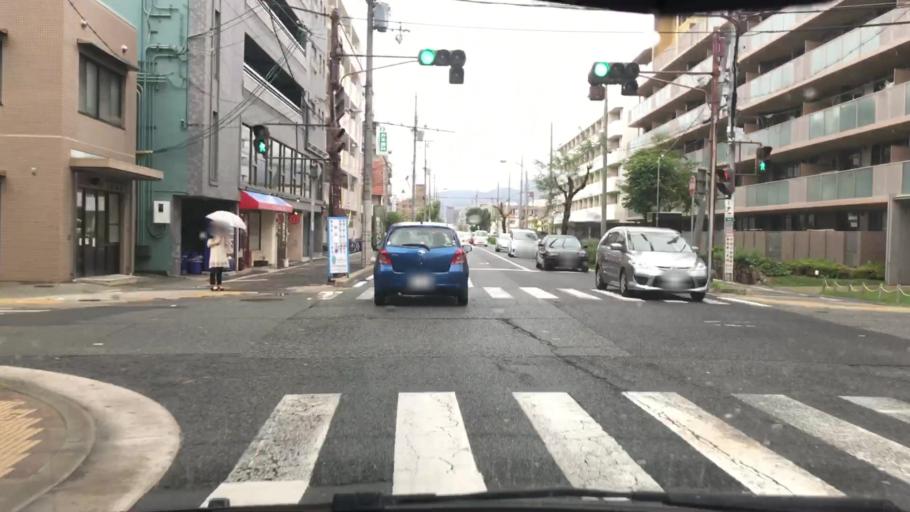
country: JP
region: Hyogo
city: Nishinomiya-hama
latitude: 34.7424
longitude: 135.3736
